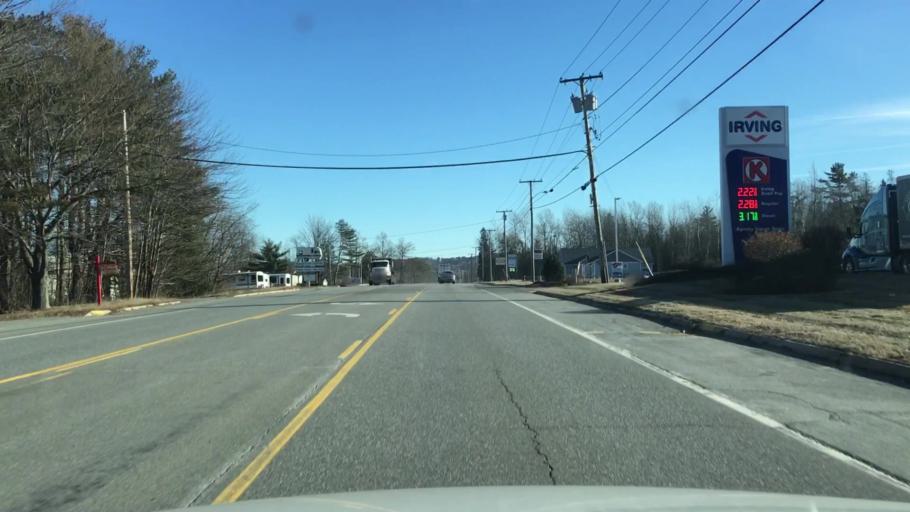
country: US
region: Maine
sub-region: Penobscot County
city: Holden
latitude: 44.7648
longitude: -68.7061
